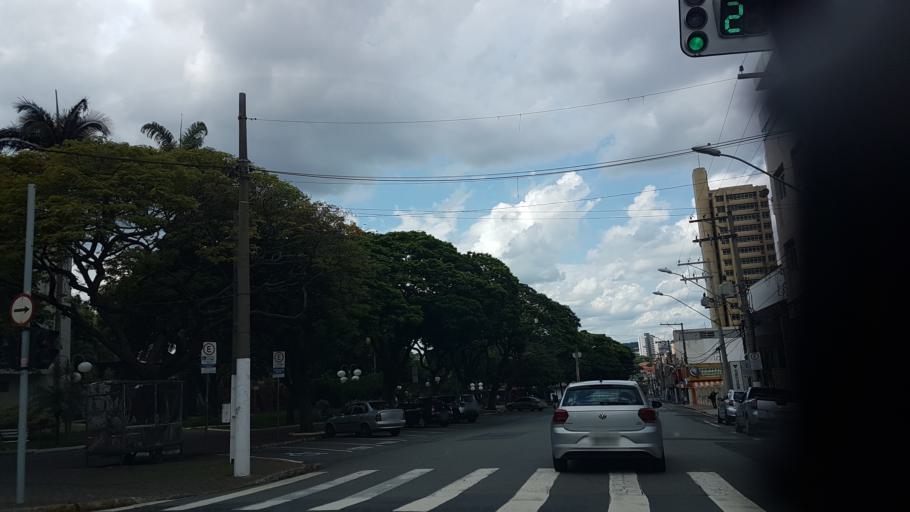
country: BR
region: Sao Paulo
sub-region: Limeira
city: Limeira
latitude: -22.5652
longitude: -47.4024
